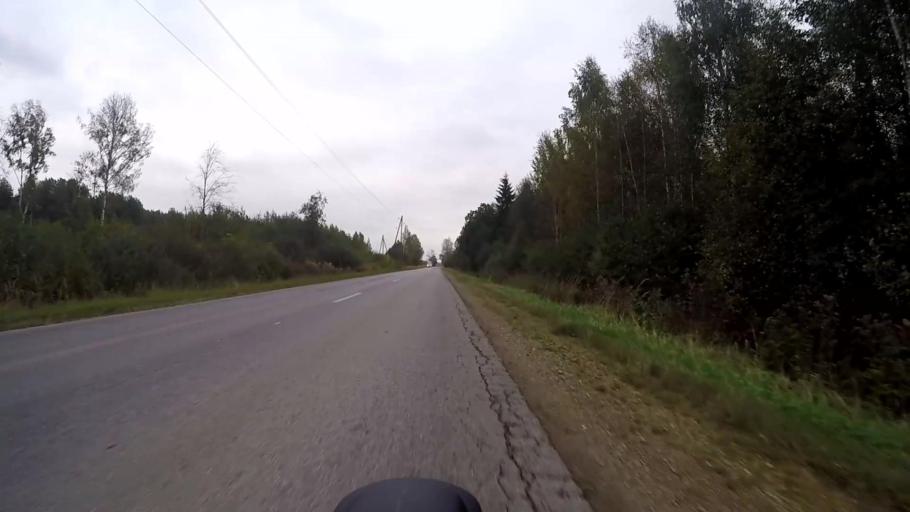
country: LV
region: Saulkrastu
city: Saulkrasti
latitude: 57.2740
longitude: 24.5213
